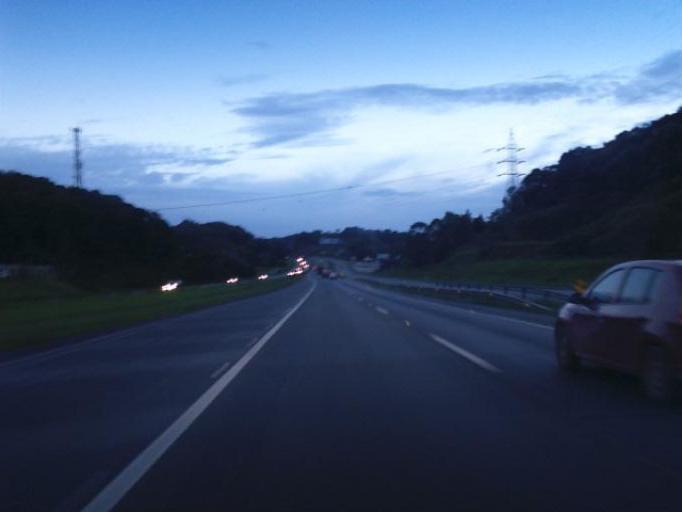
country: BR
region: Santa Catarina
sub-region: Joinville
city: Joinville
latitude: -26.3692
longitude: -48.8576
